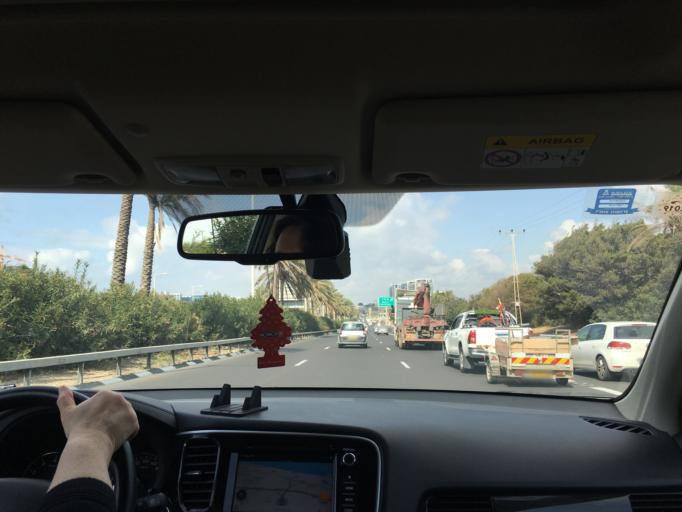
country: IL
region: Tel Aviv
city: Herzliya Pituah
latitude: 32.1523
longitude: 34.8060
